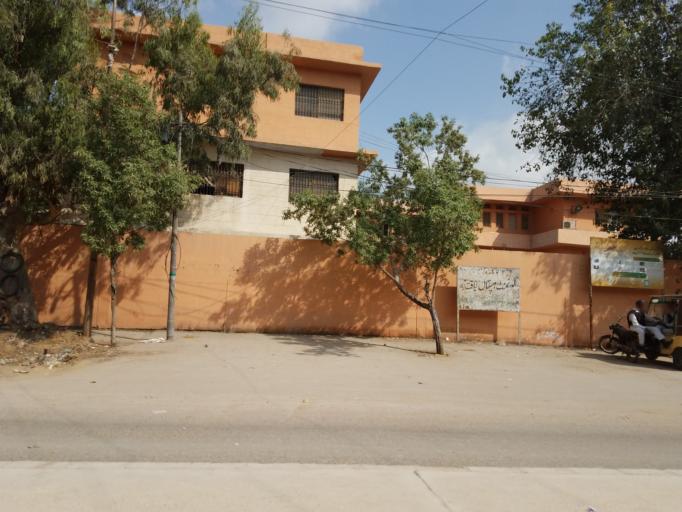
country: PK
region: Sindh
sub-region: Karachi District
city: Karachi
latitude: 24.9121
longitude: 67.0507
